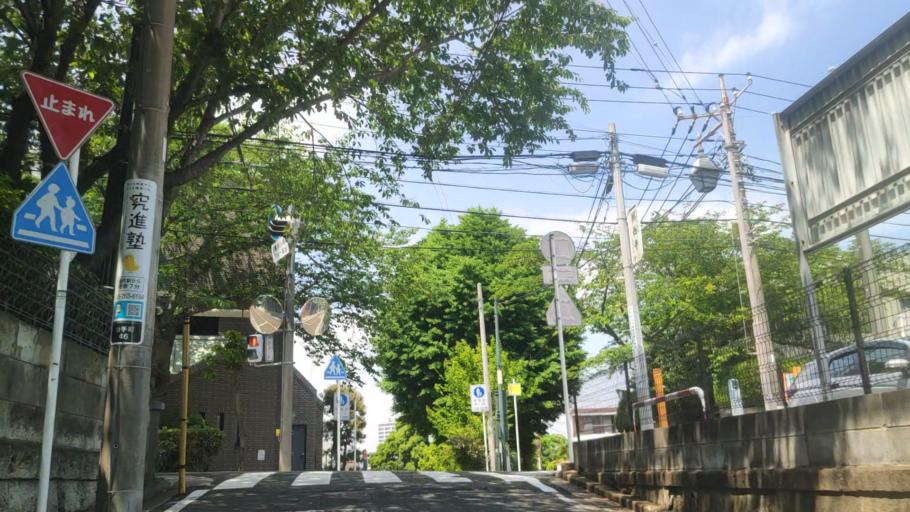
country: JP
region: Kanagawa
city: Yokohama
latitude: 35.4375
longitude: 139.6481
